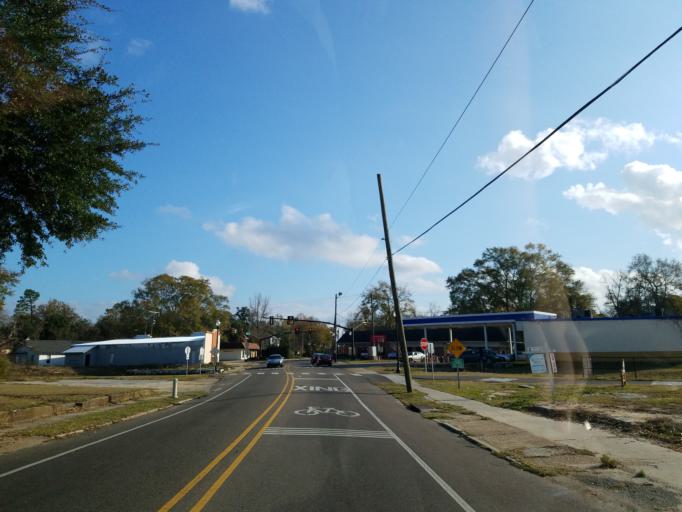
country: US
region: Mississippi
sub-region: Forrest County
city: Hattiesburg
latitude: 31.3329
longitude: -89.2972
